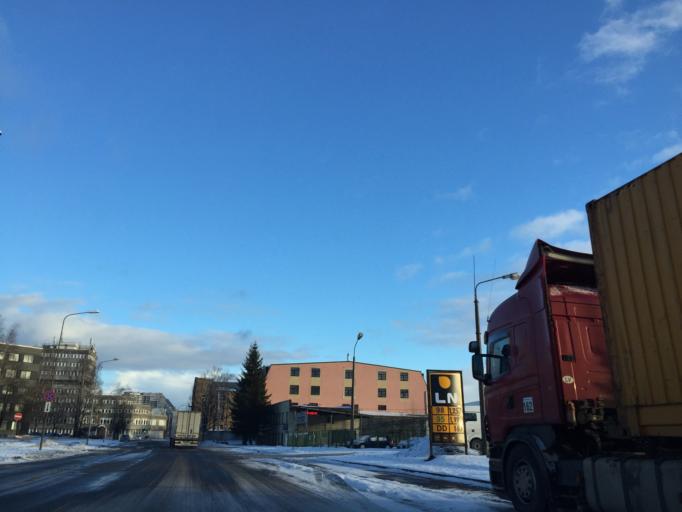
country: LV
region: Riga
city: Riga
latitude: 56.9888
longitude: 24.1181
